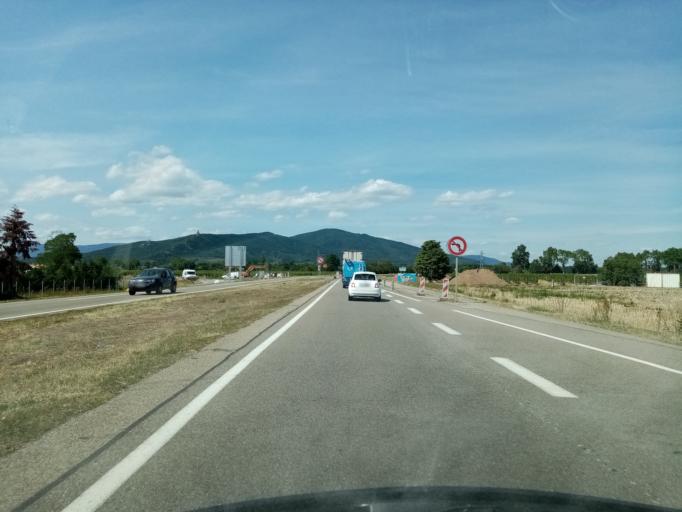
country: FR
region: Alsace
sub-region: Departement du Bas-Rhin
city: Chatenois
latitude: 48.2668
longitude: 7.4177
